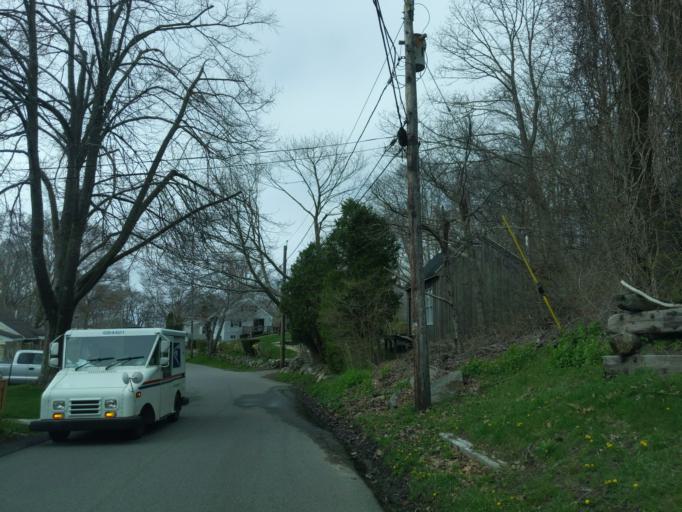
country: US
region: Massachusetts
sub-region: Essex County
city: Rockport
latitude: 42.6369
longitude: -70.6110
